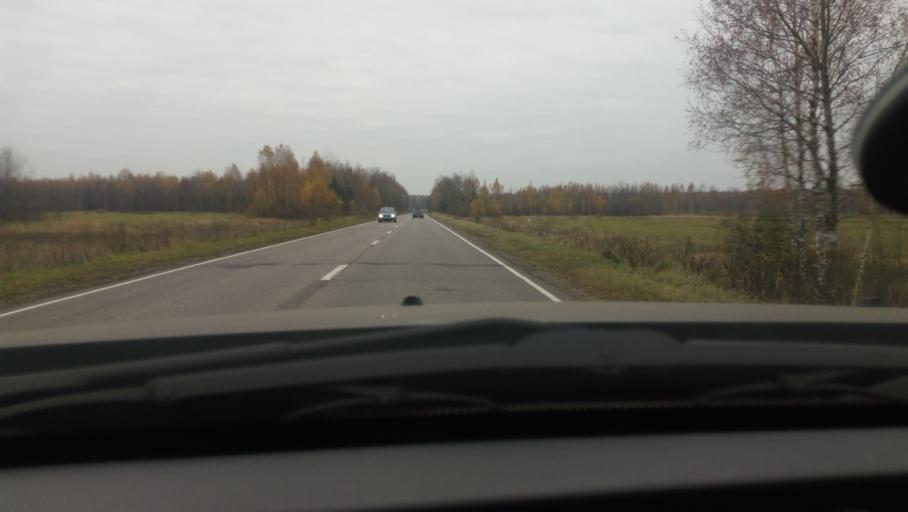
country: RU
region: Moskovskaya
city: Drezna
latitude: 55.7118
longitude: 38.8599
